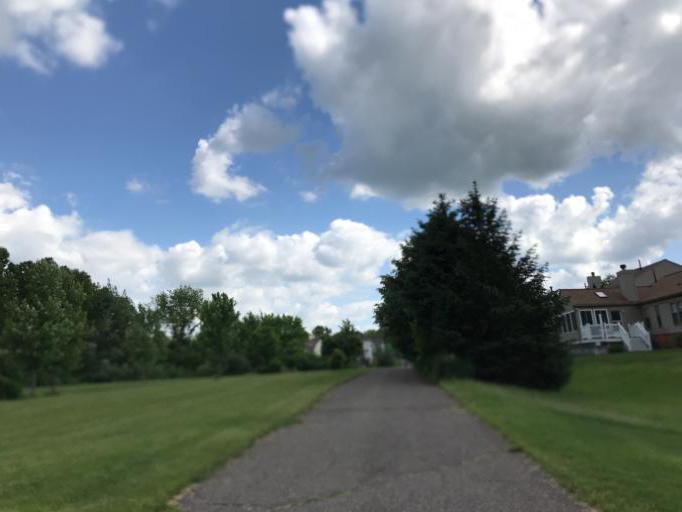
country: US
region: Michigan
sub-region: Oakland County
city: South Lyon
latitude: 42.4522
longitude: -83.6606
